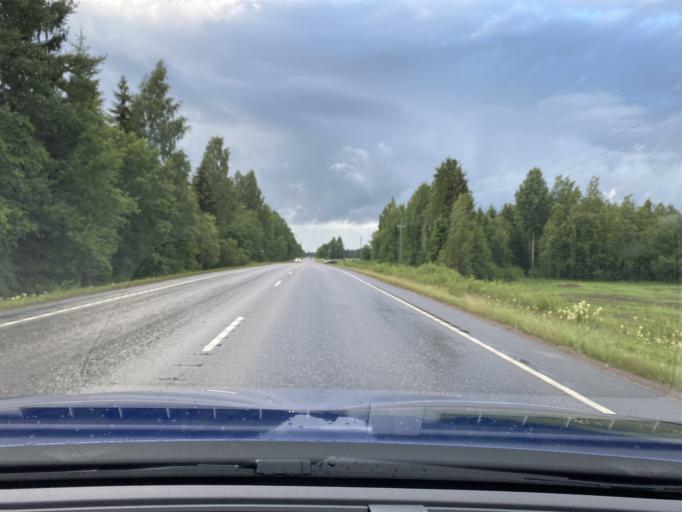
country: FI
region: Uusimaa
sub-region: Helsinki
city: Nurmijaervi
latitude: 60.5423
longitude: 24.8331
